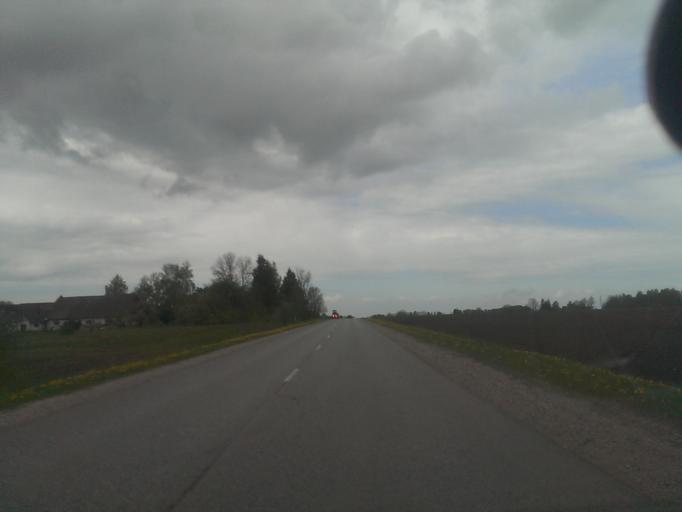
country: LV
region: Kuldigas Rajons
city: Kuldiga
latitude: 56.9883
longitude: 21.9194
